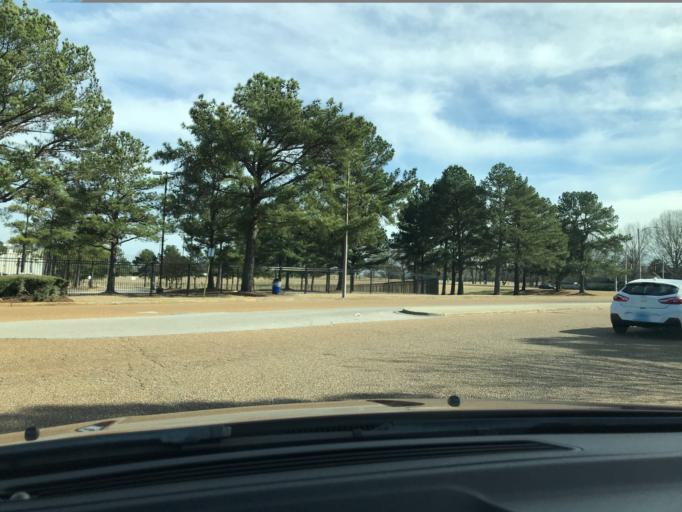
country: US
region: Tennessee
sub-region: Shelby County
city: Germantown
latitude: 35.0496
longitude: -89.7841
